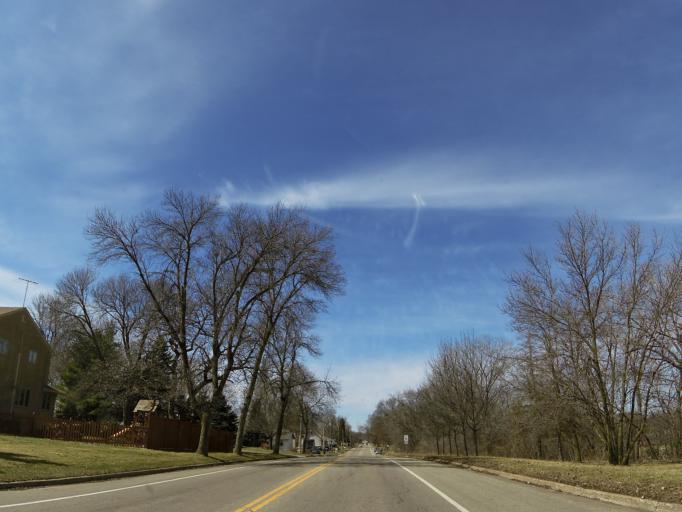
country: US
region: Minnesota
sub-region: Ramsey County
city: North Saint Paul
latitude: 44.9921
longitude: -93.0340
